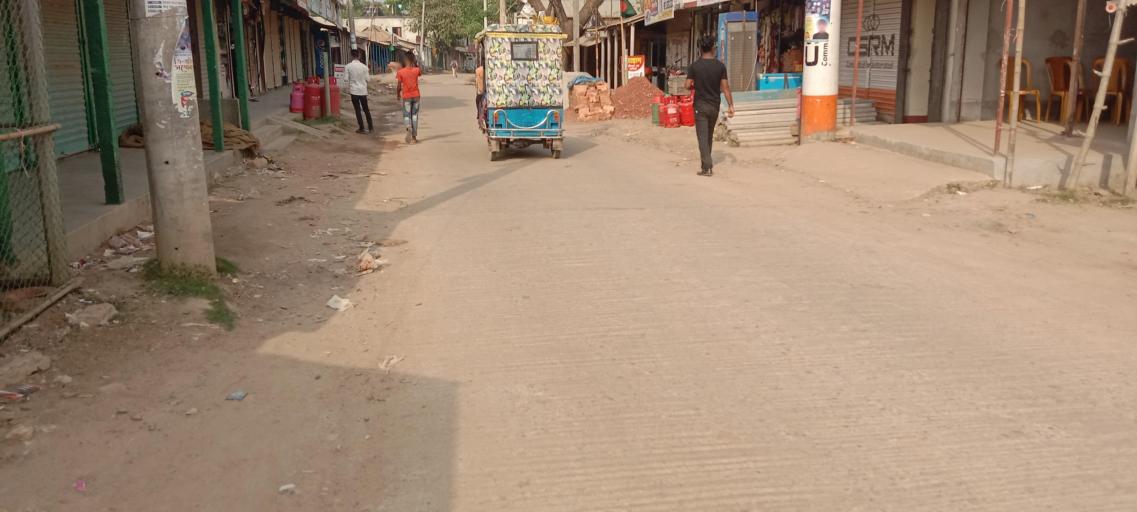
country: BD
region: Dhaka
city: Sakhipur
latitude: 24.3757
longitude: 90.3612
